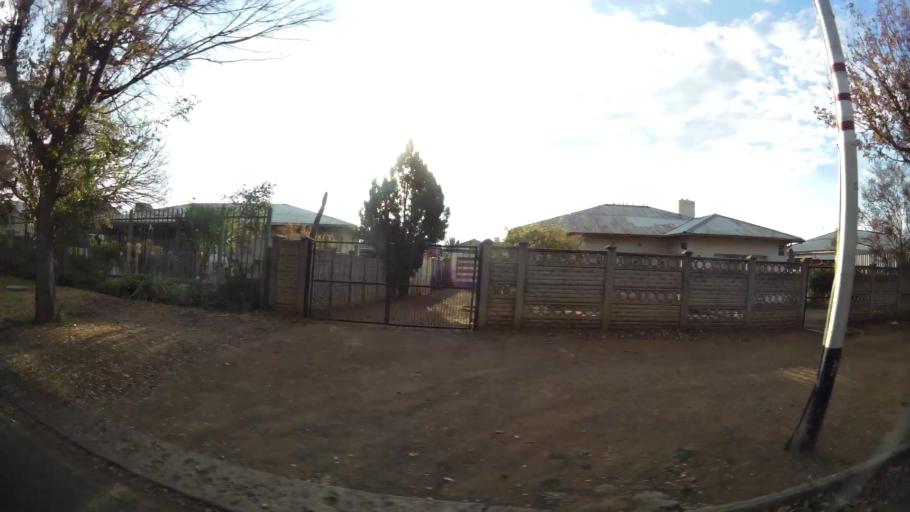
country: ZA
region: Orange Free State
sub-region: Mangaung Metropolitan Municipality
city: Bloemfontein
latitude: -29.1384
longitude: 26.1959
